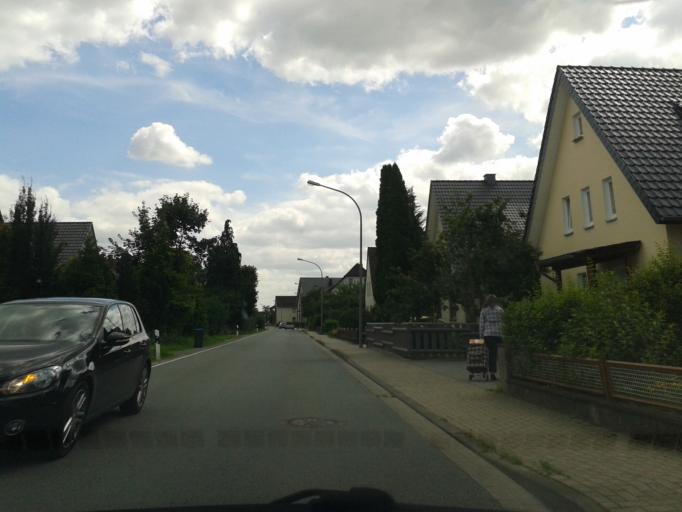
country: DE
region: North Rhine-Westphalia
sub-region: Regierungsbezirk Detmold
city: Schlangen
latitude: 51.8120
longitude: 8.8500
